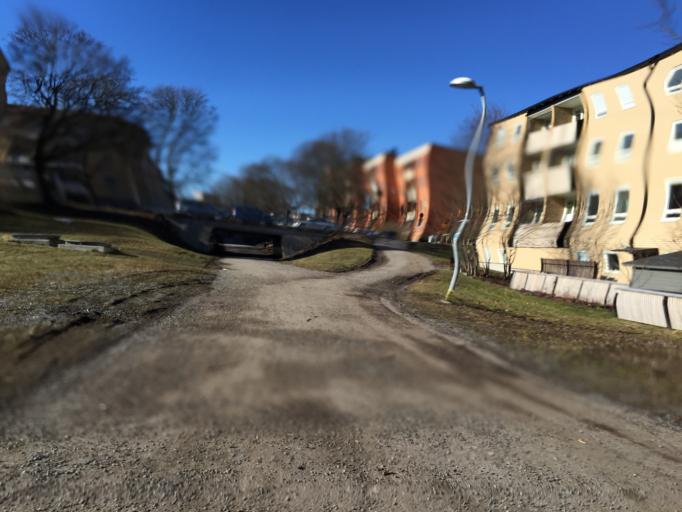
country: SE
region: Stockholm
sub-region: Stockholms Kommun
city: Bromma
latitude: 59.3637
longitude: 17.8799
